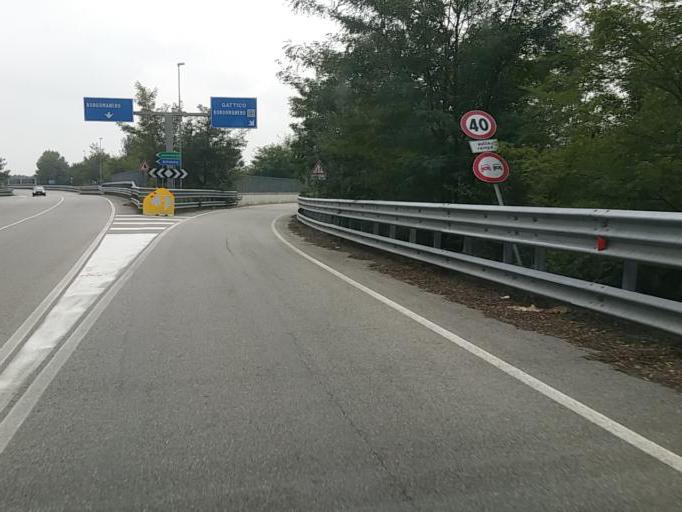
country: IT
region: Piedmont
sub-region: Provincia di Novara
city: Borgomanero
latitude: 45.7070
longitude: 8.4789
